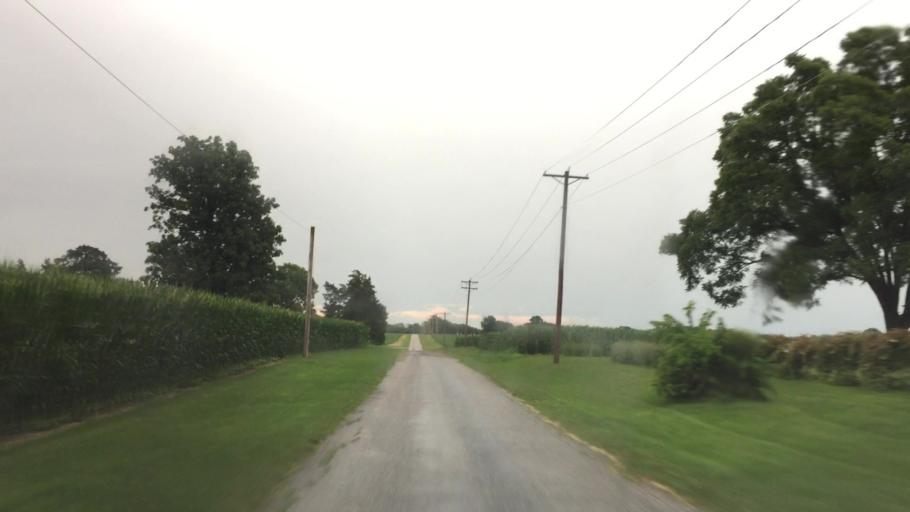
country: US
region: Illinois
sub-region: Hancock County
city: Nauvoo
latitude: 40.5495
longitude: -91.3637
